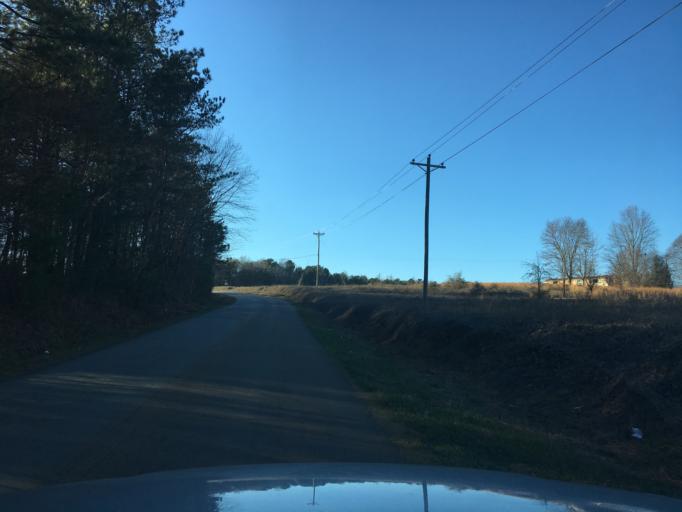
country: US
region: Georgia
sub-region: Carroll County
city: Carrollton
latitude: 33.4399
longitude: -85.1196
